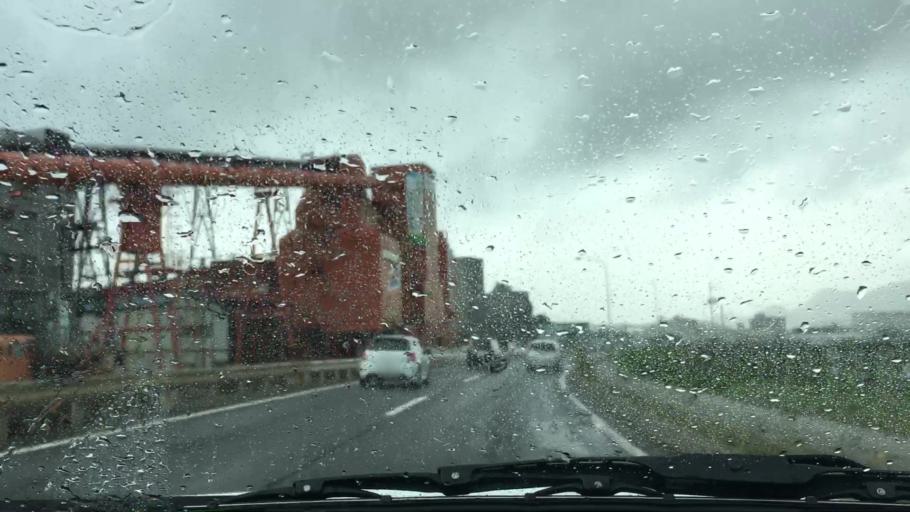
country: JP
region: Hokkaido
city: Sapporo
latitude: 43.0128
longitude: 141.3542
